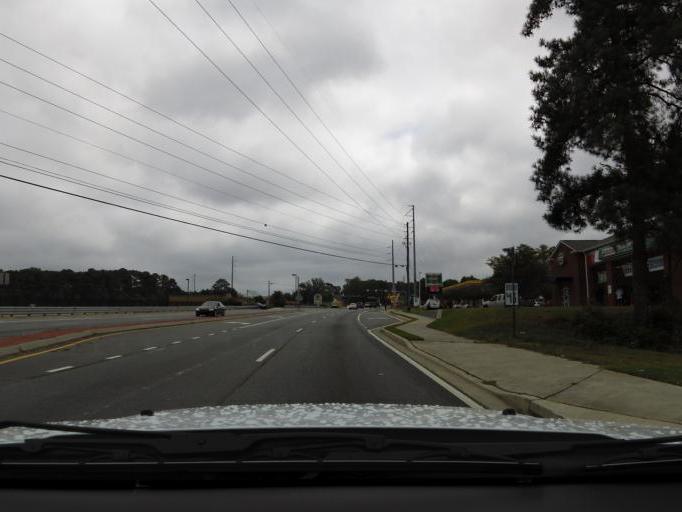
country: US
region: Georgia
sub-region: Cobb County
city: Kennesaw
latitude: 34.0479
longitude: -84.6030
